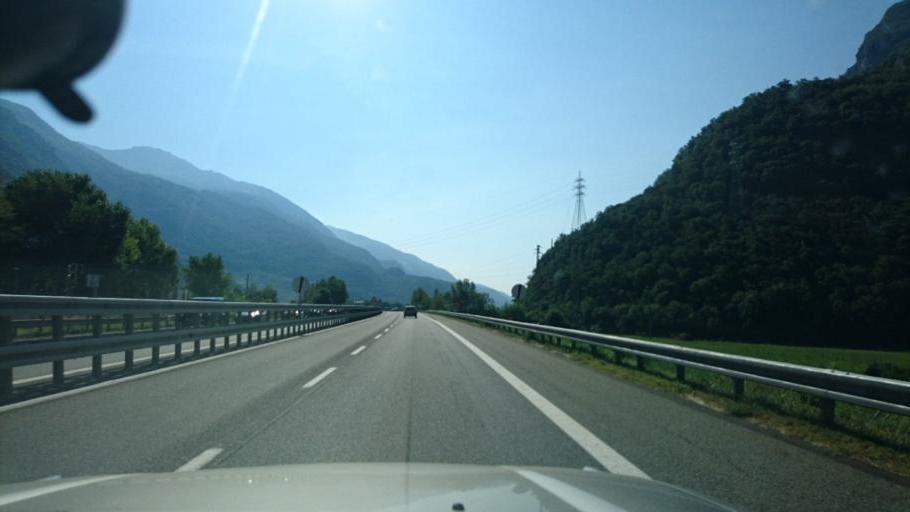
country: IT
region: Aosta Valley
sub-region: Valle d'Aosta
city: Pont-Saint-Martin
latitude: 45.5921
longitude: 7.7894
